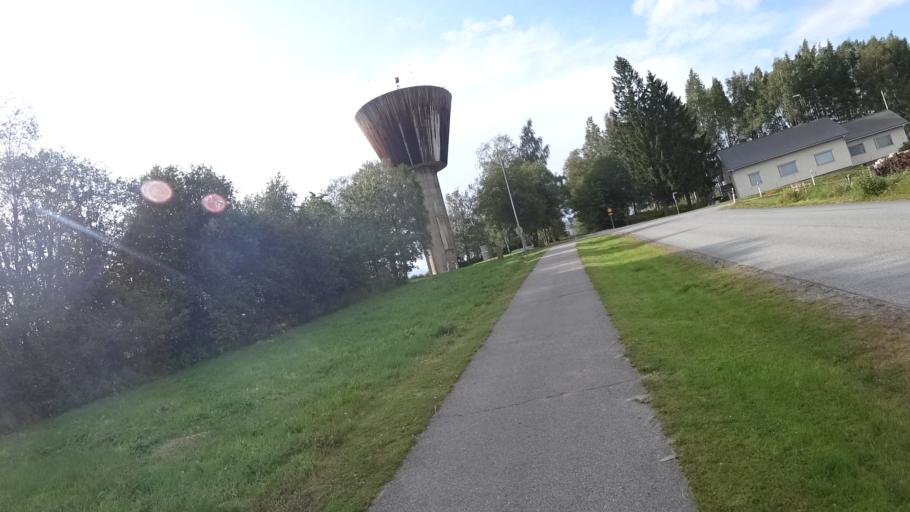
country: FI
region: North Karelia
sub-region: Joensuu
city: Ilomantsi
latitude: 62.6706
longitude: 30.9208
